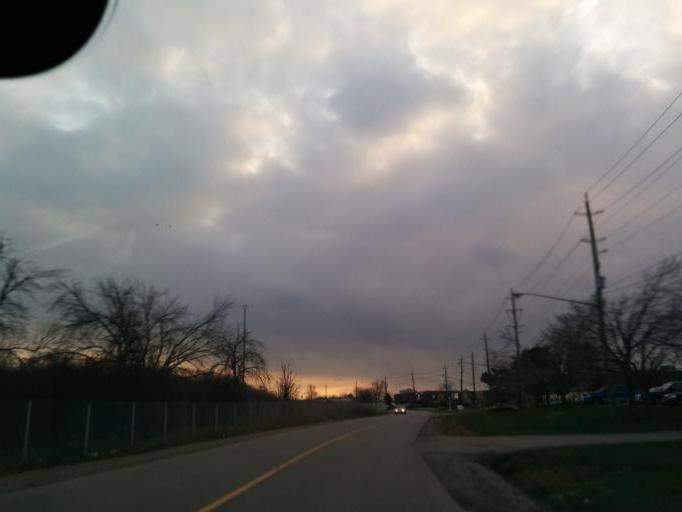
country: CA
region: Ontario
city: Oakville
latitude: 43.4731
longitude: -79.6742
